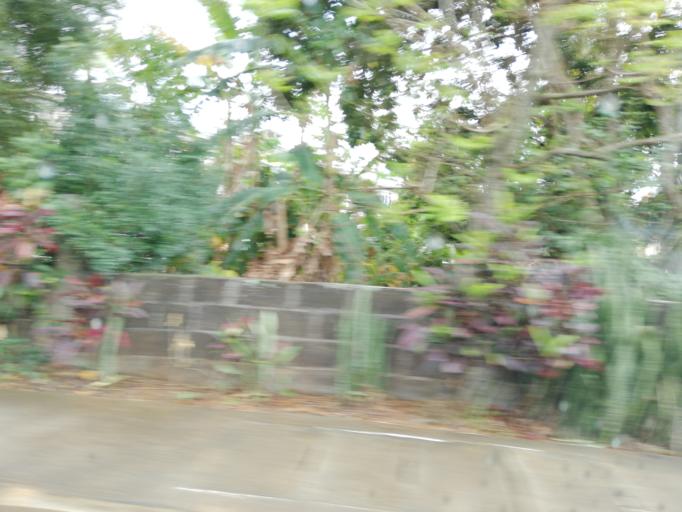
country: MU
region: Pamplemousses
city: Pamplemousses
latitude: -20.1127
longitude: 57.5646
